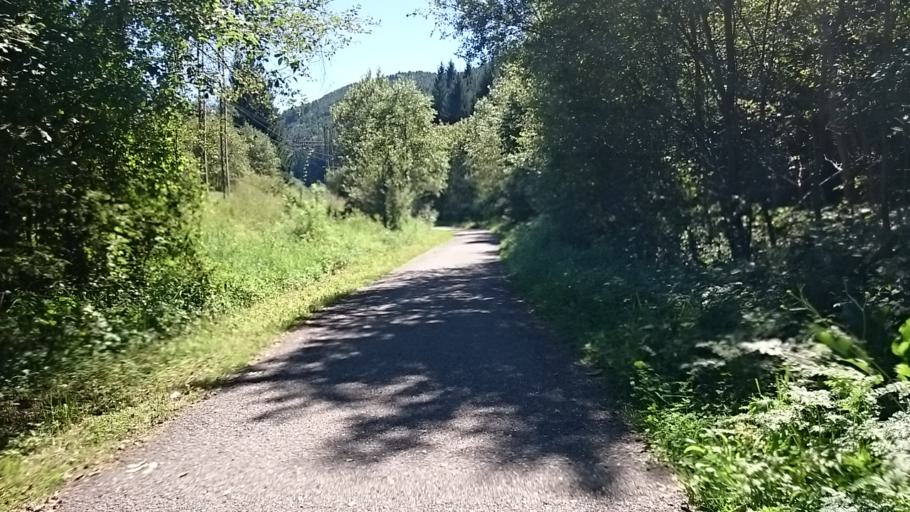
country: IT
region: Trentino-Alto Adige
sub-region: Bolzano
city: Terento
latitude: 46.8070
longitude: 11.8056
